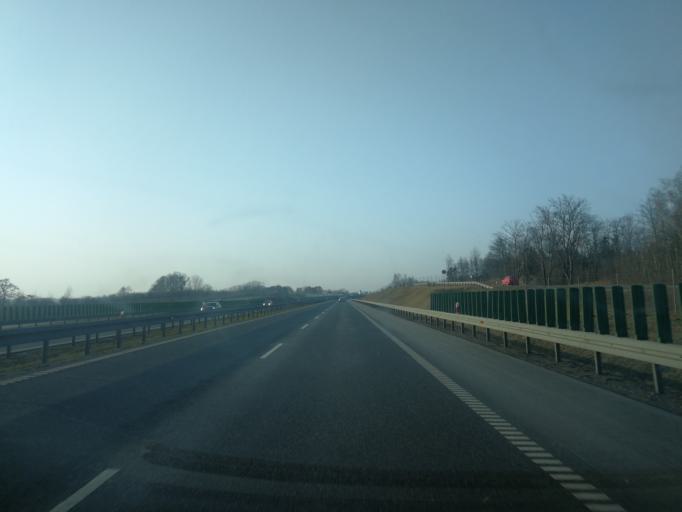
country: PL
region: Warmian-Masurian Voivodeship
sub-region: Powiat elblaski
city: Gronowo Gorne
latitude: 54.1208
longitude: 19.4698
